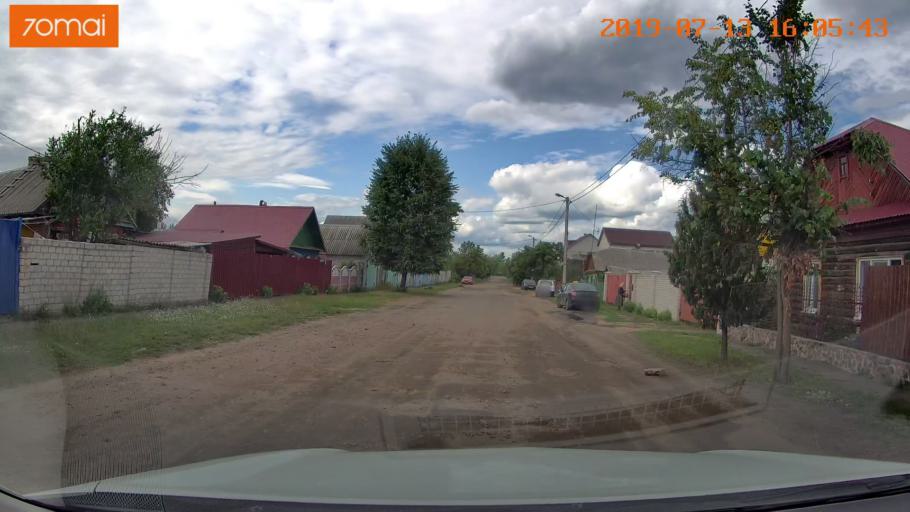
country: BY
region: Mogilev
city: Babruysk
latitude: 53.1501
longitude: 29.2050
